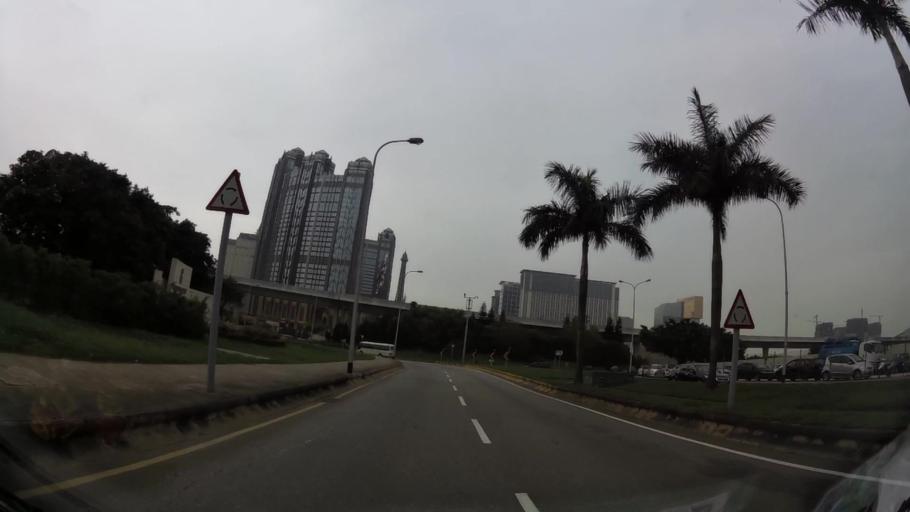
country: MO
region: Macau
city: Macau
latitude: 22.1376
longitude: 113.5631
